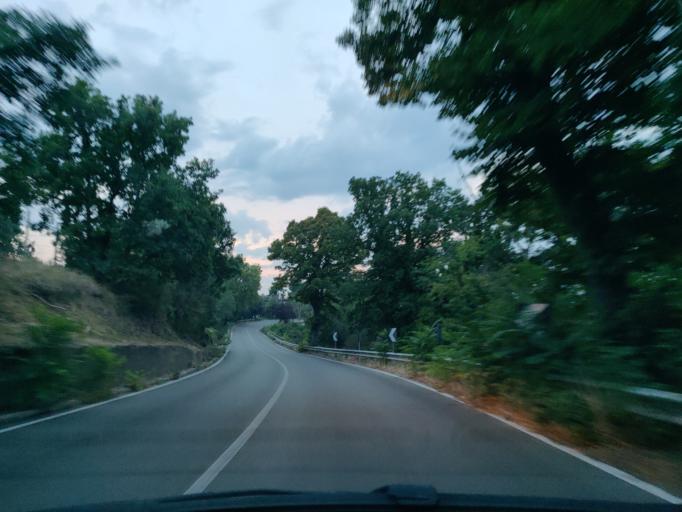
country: IT
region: Latium
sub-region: Provincia di Viterbo
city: San Martino al Cimino
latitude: 42.3835
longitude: 12.0802
